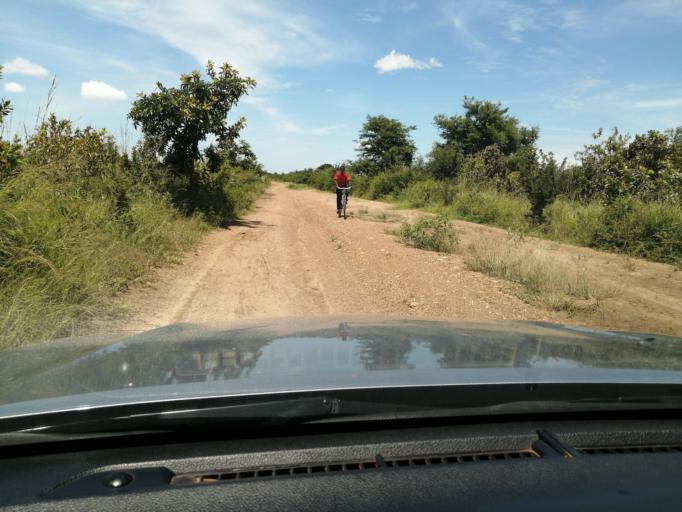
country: ZM
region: Central
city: Chibombo
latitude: -15.0695
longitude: 27.8338
